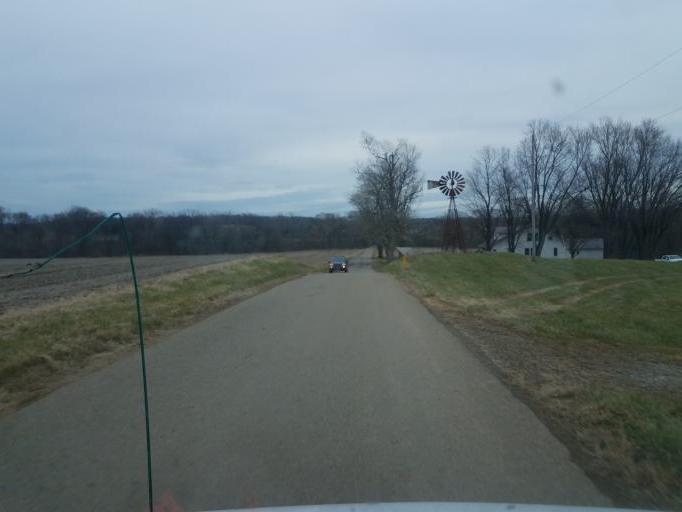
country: US
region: Ohio
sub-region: Licking County
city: Utica
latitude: 40.2448
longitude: -82.4579
